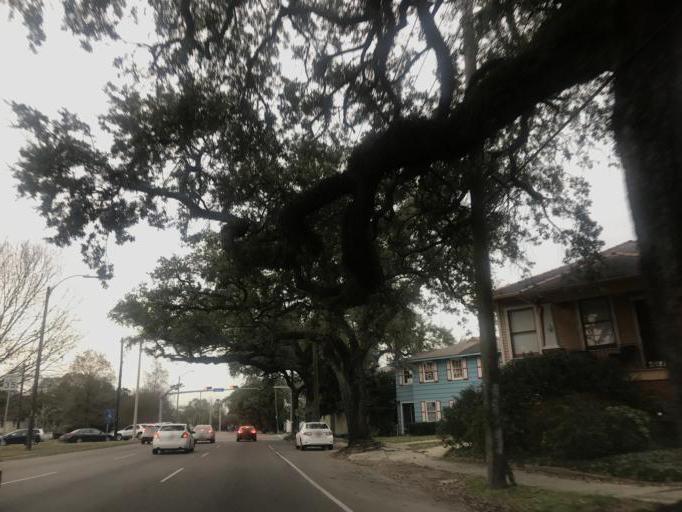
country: US
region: Louisiana
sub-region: Jefferson Parish
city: Jefferson
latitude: 29.9506
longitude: -90.1155
